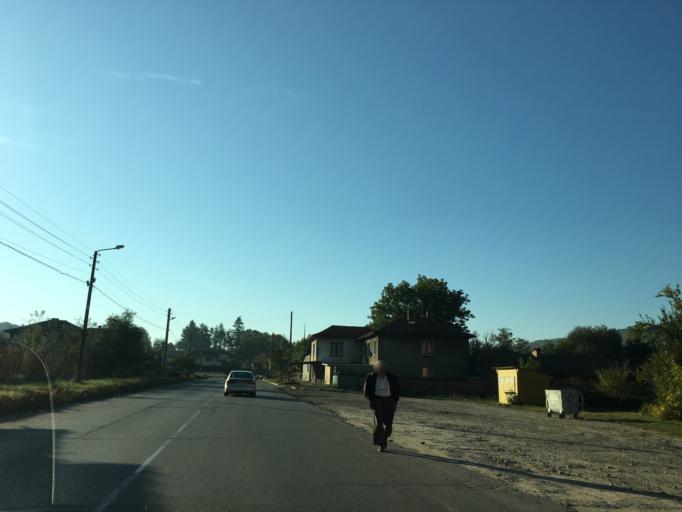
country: BG
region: Sofiya
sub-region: Obshtina Ikhtiman
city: Ikhtiman
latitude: 42.3874
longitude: 23.8730
